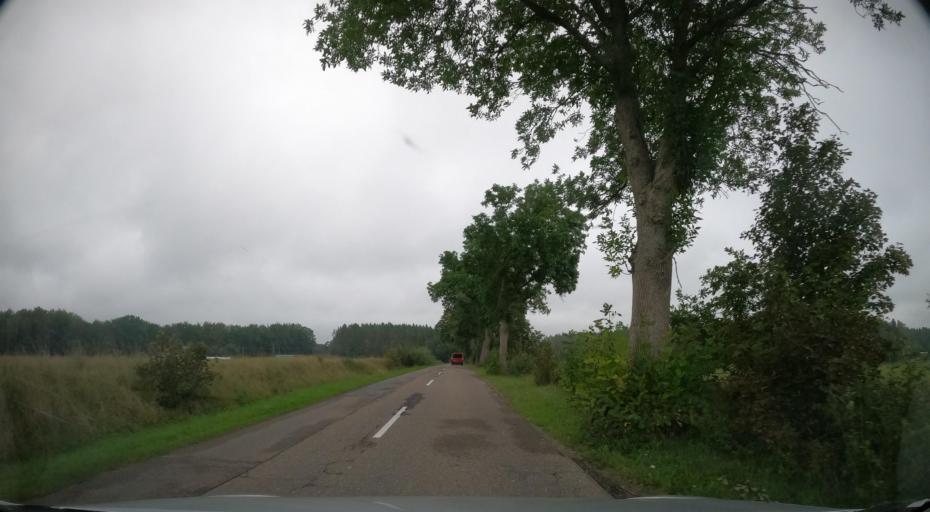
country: PL
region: Pomeranian Voivodeship
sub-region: Powiat wejherowski
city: Luzino
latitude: 54.4874
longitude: 18.1142
